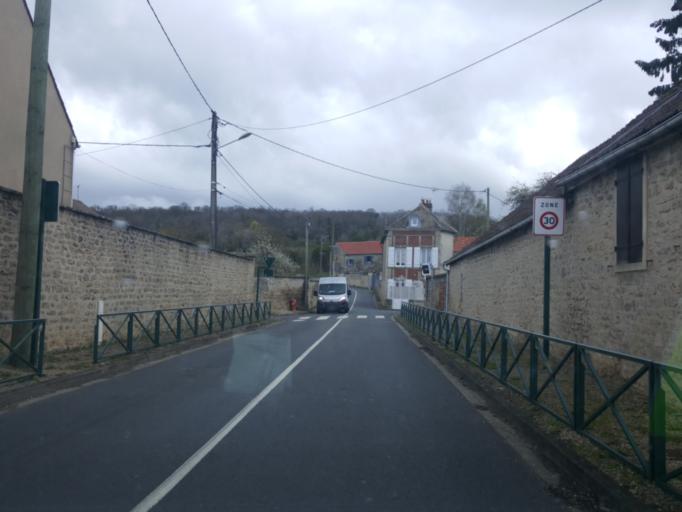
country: FR
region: Ile-de-France
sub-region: Departement du Val-d'Oise
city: Magny-en-Vexin
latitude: 49.1636
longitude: 1.7801
